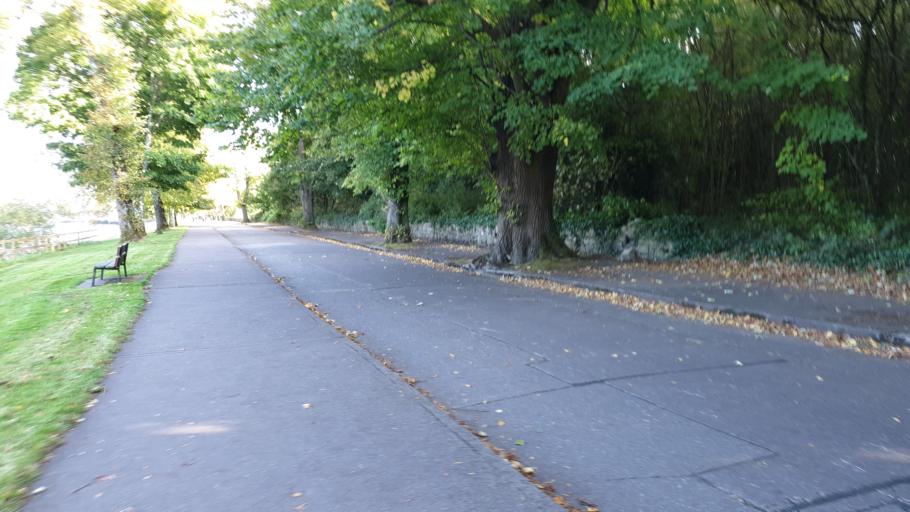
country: IE
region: Munster
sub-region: County Cork
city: Cork
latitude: 51.8994
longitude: -8.4241
